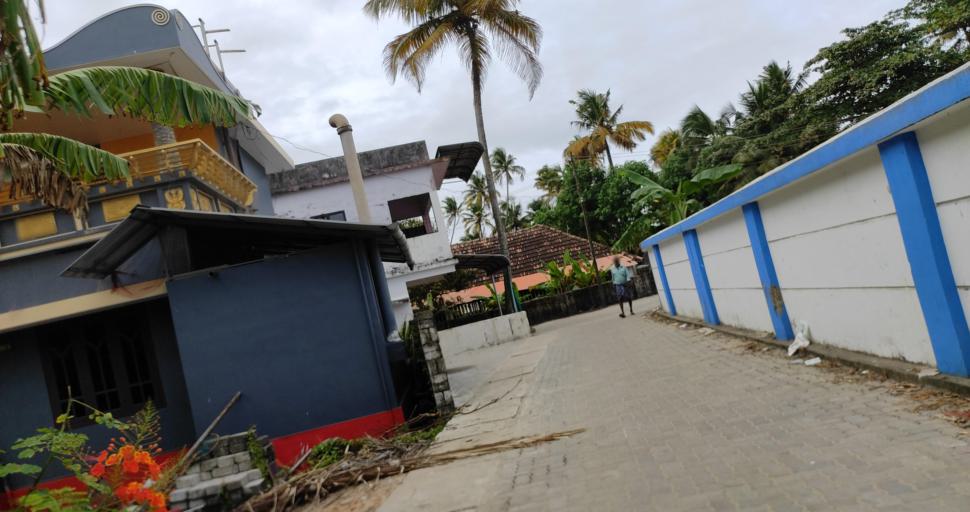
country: IN
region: Kerala
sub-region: Alappuzha
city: Kutiatodu
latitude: 9.7986
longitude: 76.2759
